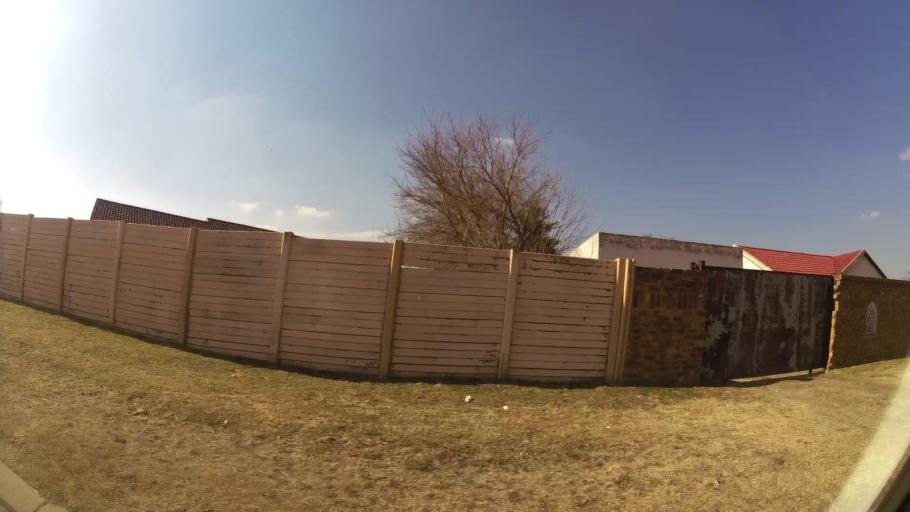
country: ZA
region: Gauteng
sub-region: Ekurhuleni Metropolitan Municipality
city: Benoni
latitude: -26.2466
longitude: 28.3107
